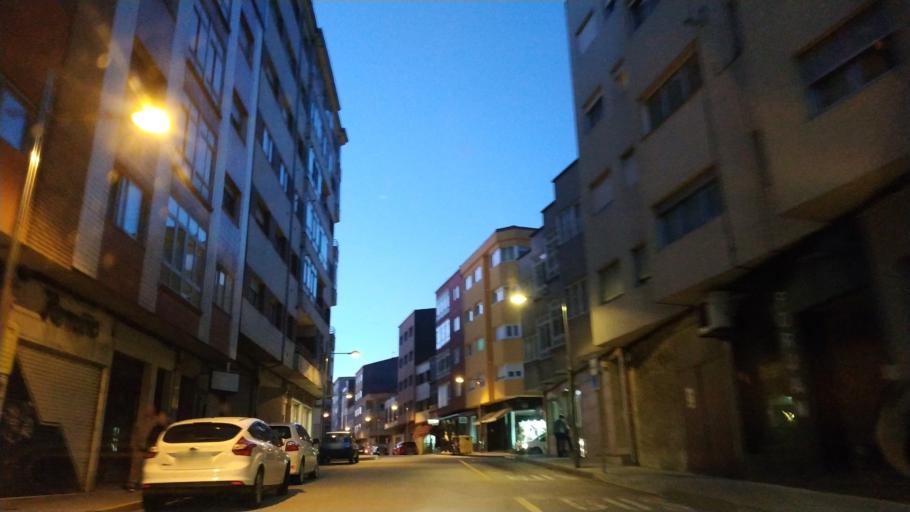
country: ES
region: Galicia
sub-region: Provincia da Coruna
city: Negreira
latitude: 42.9105
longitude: -8.7353
